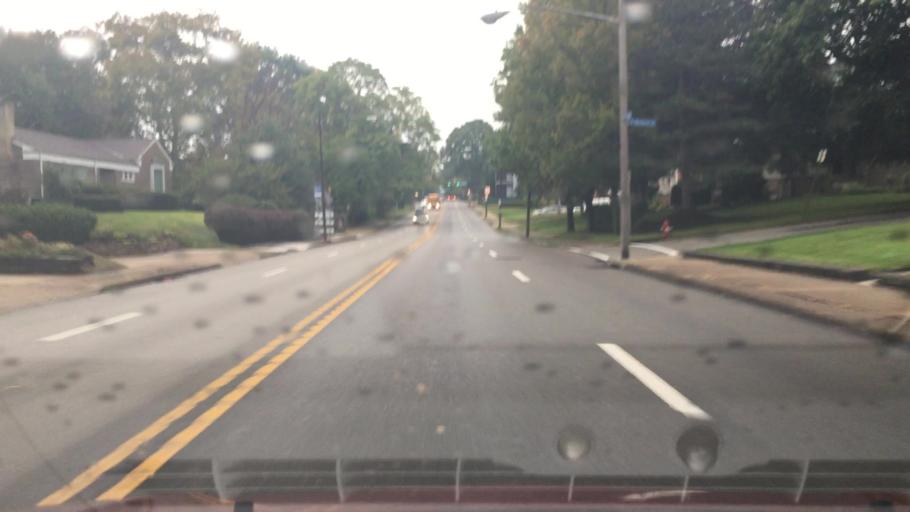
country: US
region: Pennsylvania
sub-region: Allegheny County
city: Wilkinsburg
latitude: 40.4509
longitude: -79.9066
